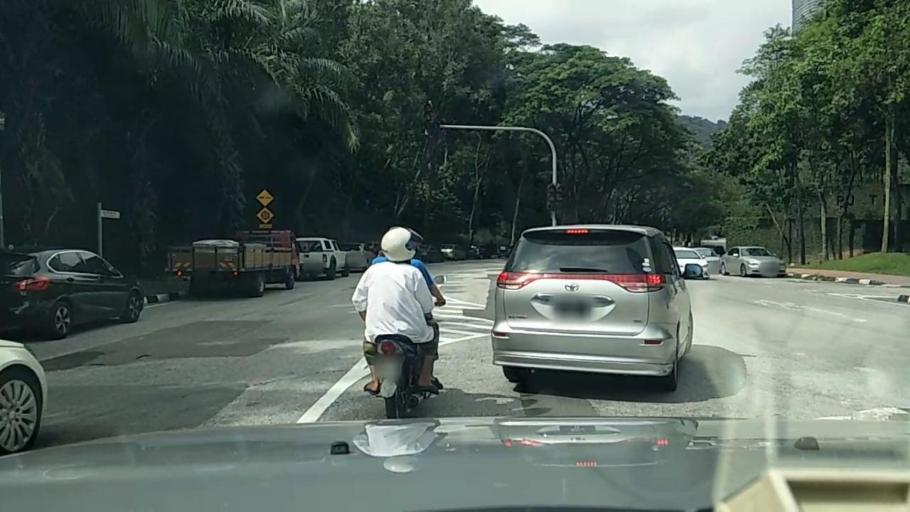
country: MY
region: Selangor
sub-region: Petaling
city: Petaling Jaya
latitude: 3.1681
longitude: 101.6124
